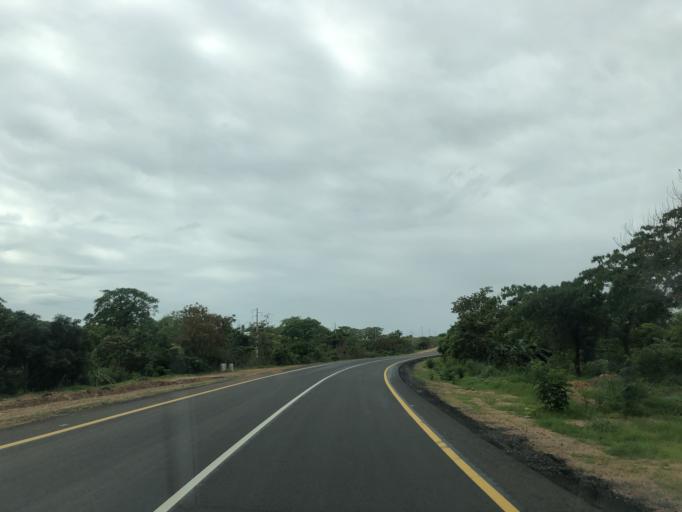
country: AO
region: Cuanza Norte
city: N'dalatando
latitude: -9.4344
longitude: 14.3090
